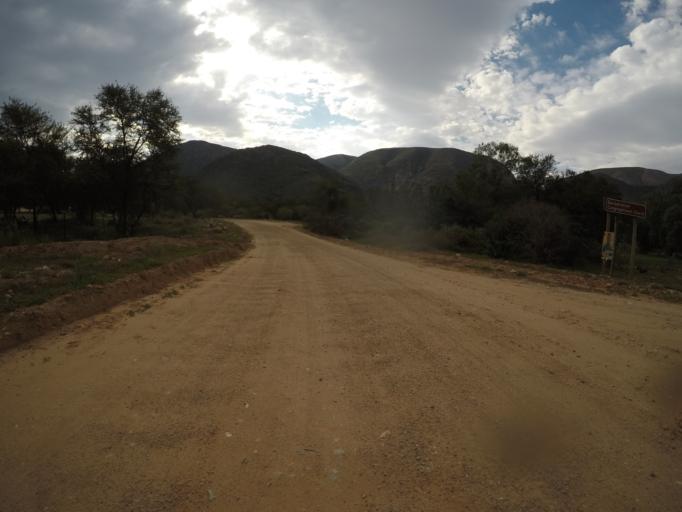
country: ZA
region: Eastern Cape
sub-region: Cacadu District Municipality
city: Kareedouw
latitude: -33.5836
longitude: 24.1657
